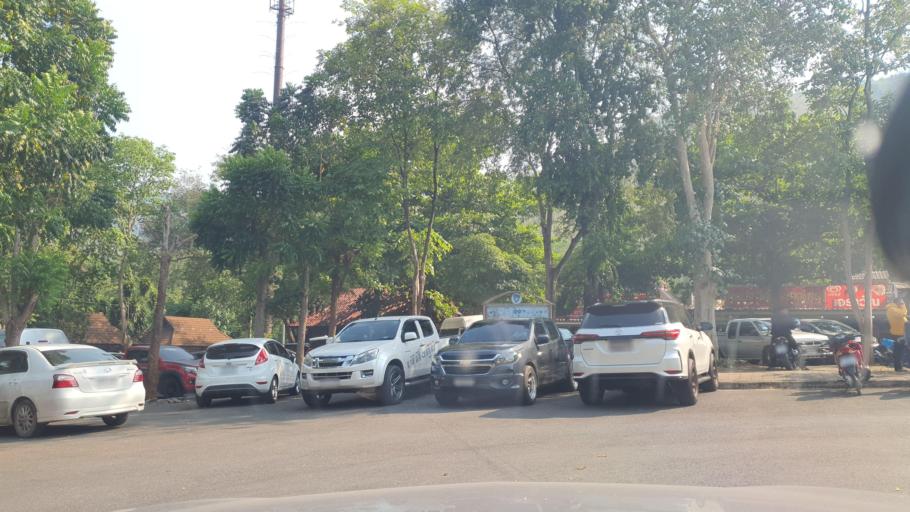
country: TH
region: Kanchanaburi
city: Si Sawat
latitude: 14.3749
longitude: 99.1444
